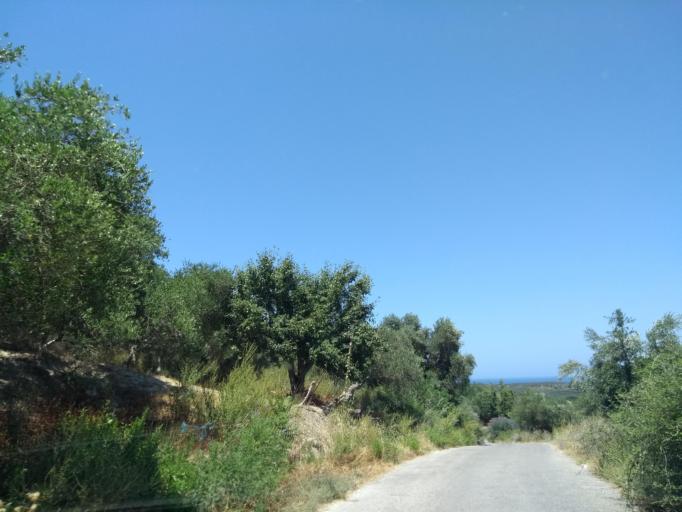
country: GR
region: Crete
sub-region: Nomos Chanias
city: Georgioupolis
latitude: 35.3206
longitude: 24.3124
